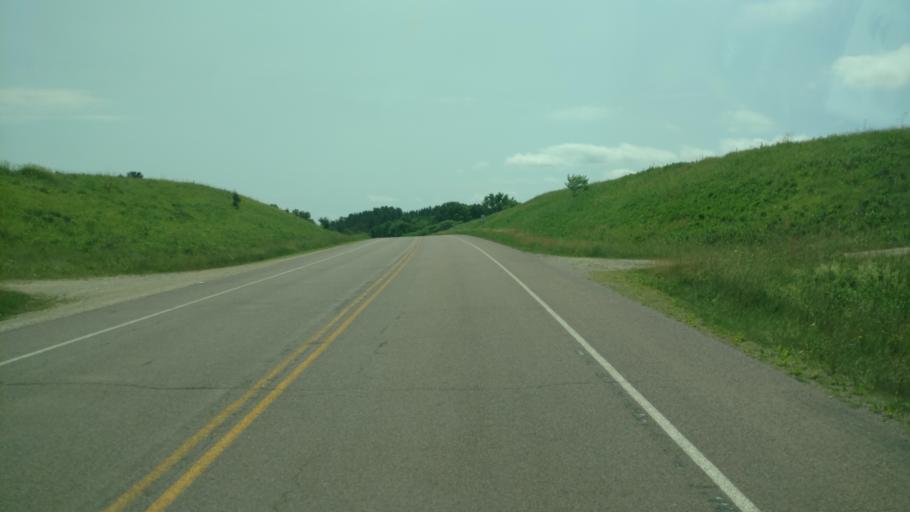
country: US
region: Wisconsin
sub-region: Monroe County
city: Cashton
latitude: 43.6562
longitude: -90.5927
